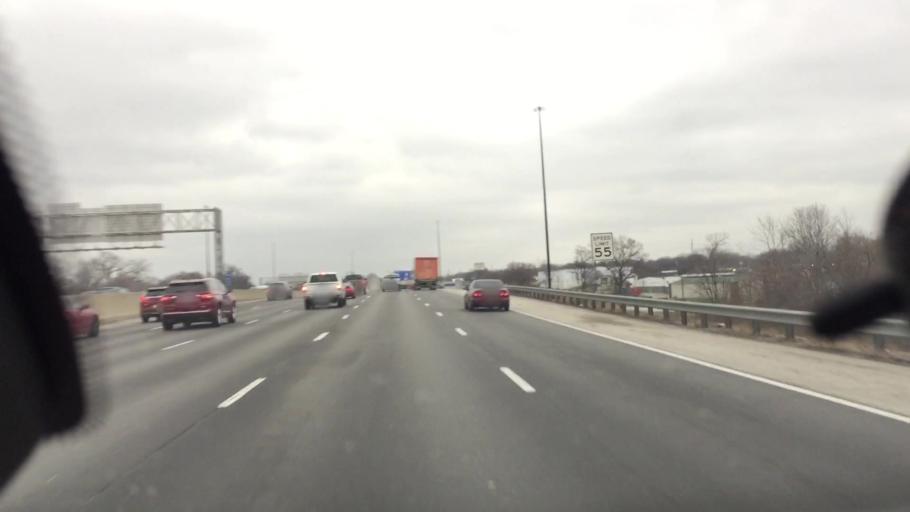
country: US
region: Indiana
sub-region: Marion County
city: Indianapolis
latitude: 39.7863
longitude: -86.1358
